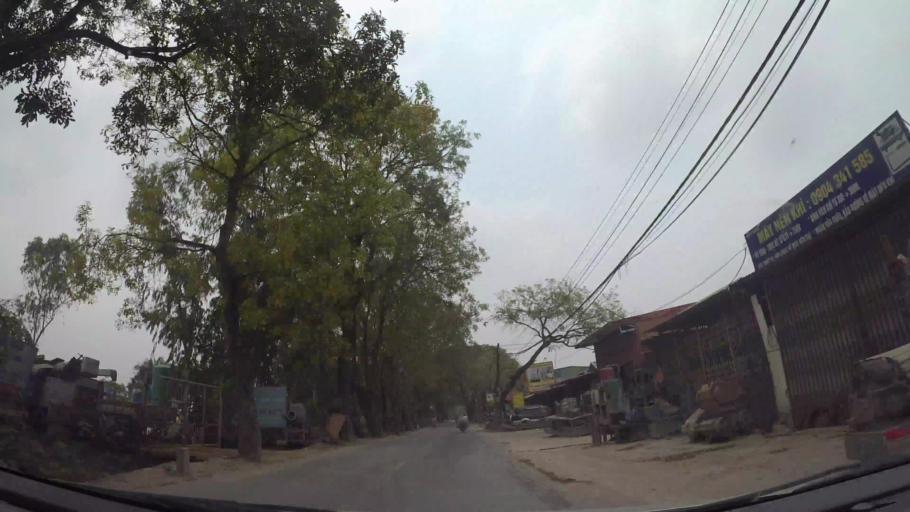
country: VN
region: Ha Noi
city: Cau Dien
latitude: 21.0177
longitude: 105.7447
